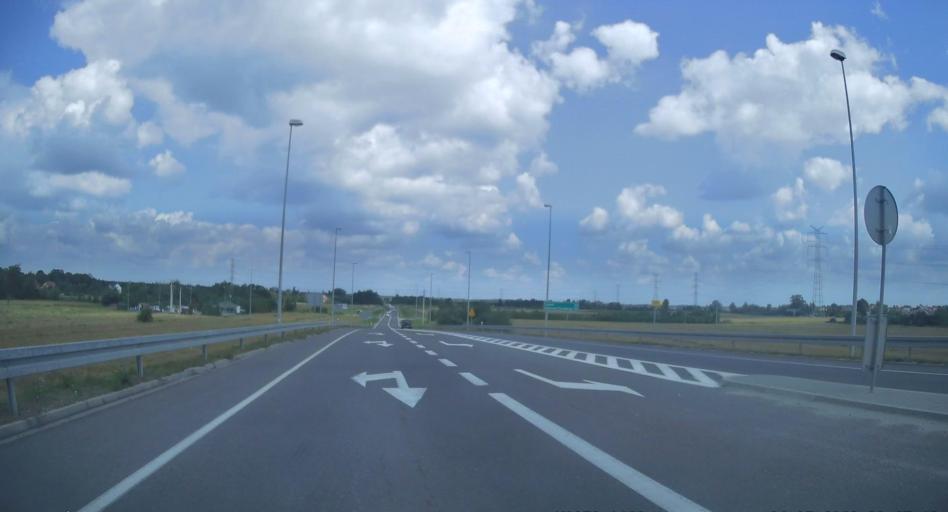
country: PL
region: Lesser Poland Voivodeship
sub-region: Powiat tarnowski
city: Wojnicz
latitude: 49.9642
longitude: 20.8488
